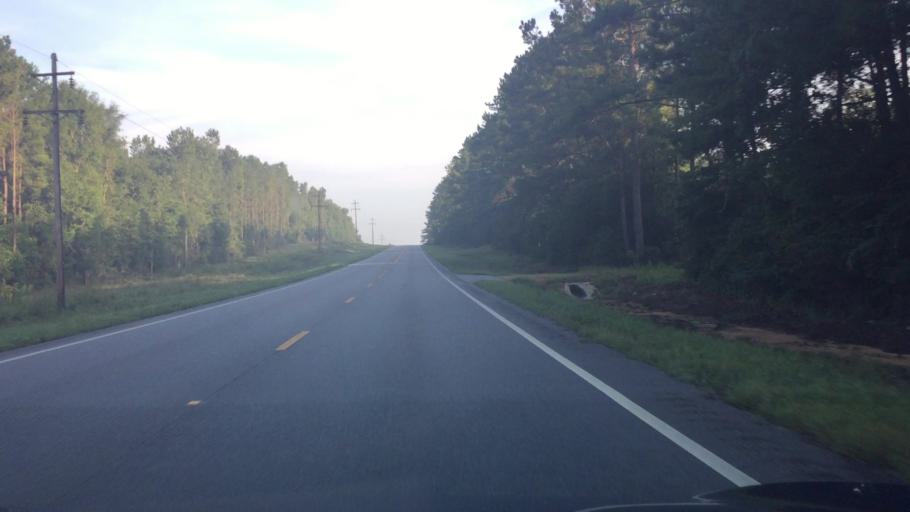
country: US
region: Alabama
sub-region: Covington County
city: Florala
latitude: 31.0610
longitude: -86.3949
